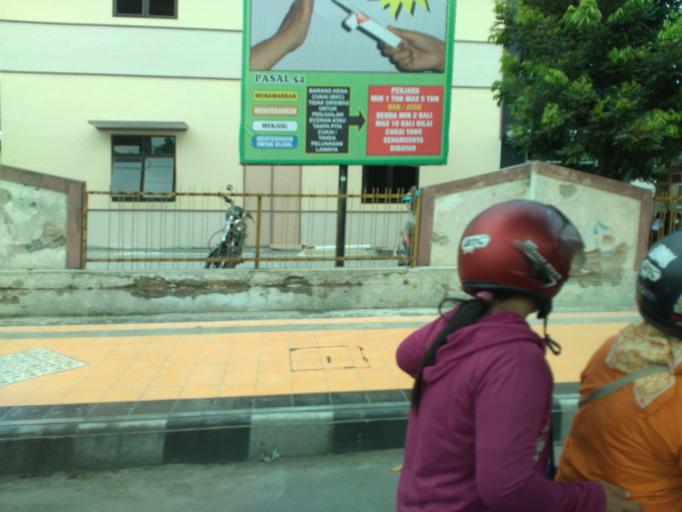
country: ID
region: Central Java
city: Klaten
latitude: -7.6931
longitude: 110.6111
